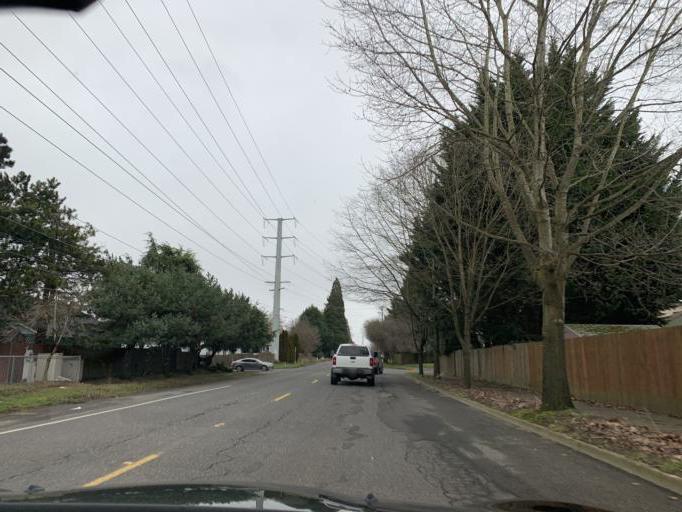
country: US
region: Washington
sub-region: Clark County
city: Mill Plain
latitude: 45.6212
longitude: -122.4940
